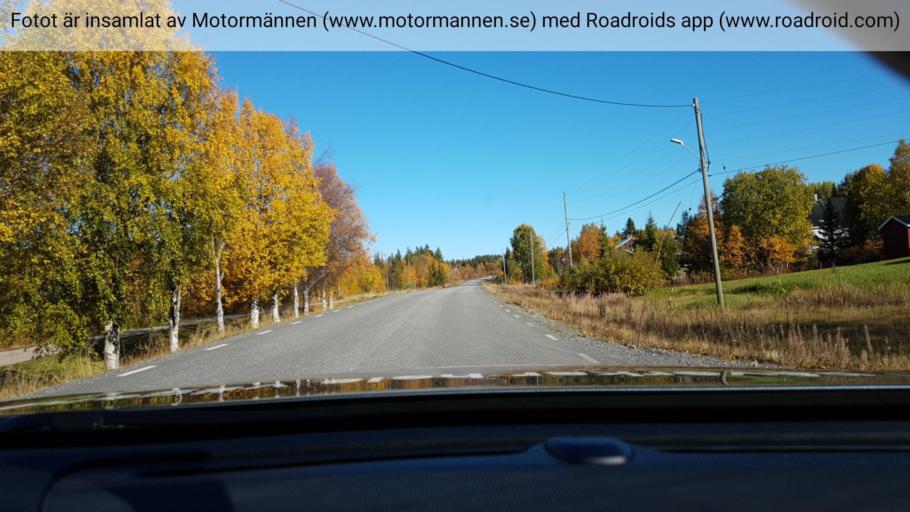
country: SE
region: Norrbotten
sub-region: Gallivare Kommun
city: Gaellivare
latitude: 66.7632
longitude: 21.0284
